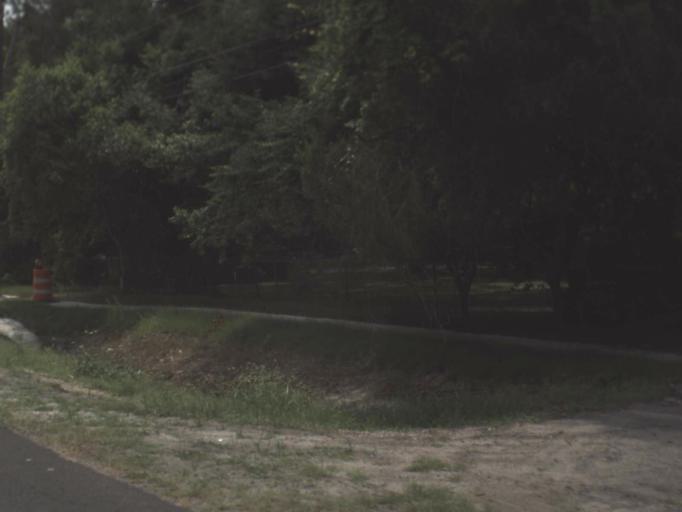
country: US
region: Florida
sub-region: Nassau County
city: Nassau Village-Ratliff
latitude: 30.4379
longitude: -81.7465
